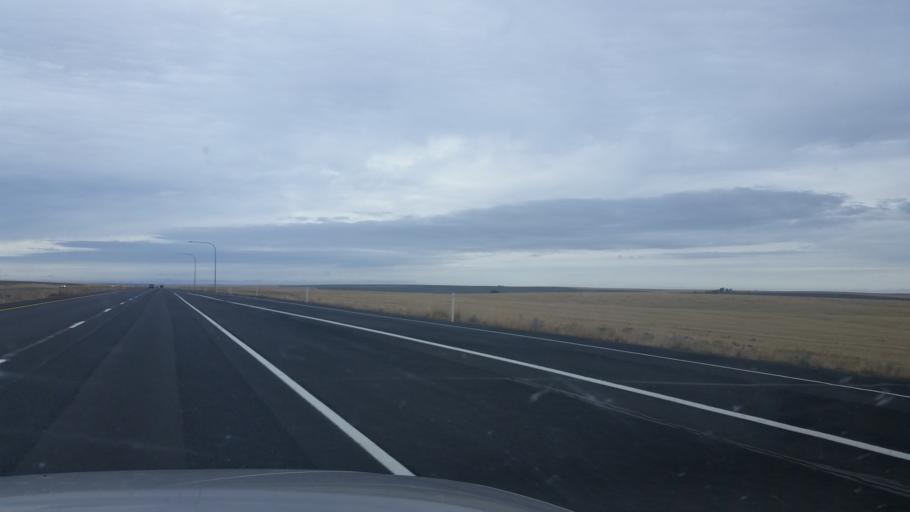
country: US
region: Washington
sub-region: Adams County
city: Ritzville
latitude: 47.1112
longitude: -118.4995
